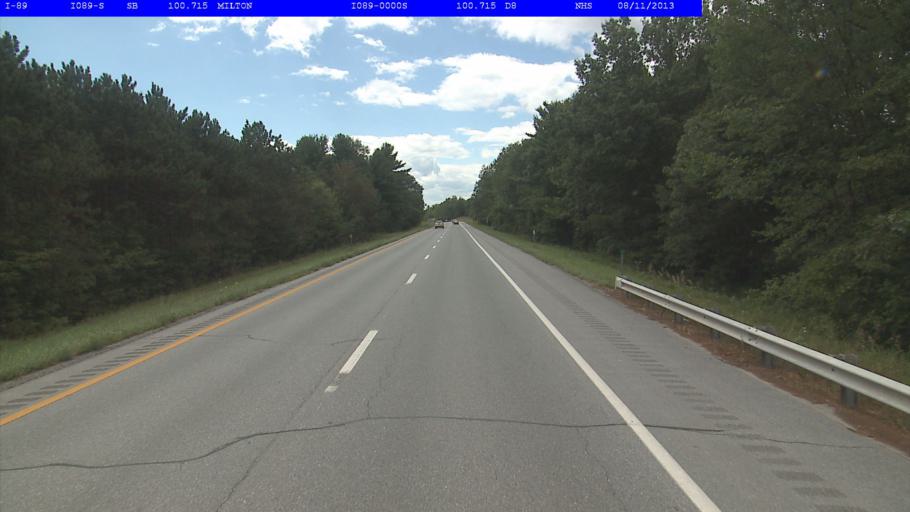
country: US
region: Vermont
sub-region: Chittenden County
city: Milton
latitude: 44.6272
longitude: -73.1525
